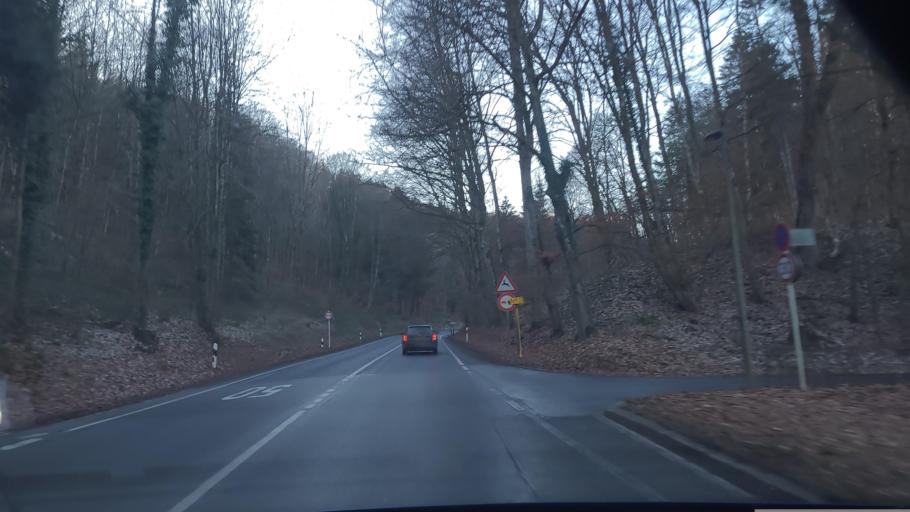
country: LU
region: Luxembourg
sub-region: Canton de Luxembourg
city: Strassen
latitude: 49.6269
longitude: 6.1006
